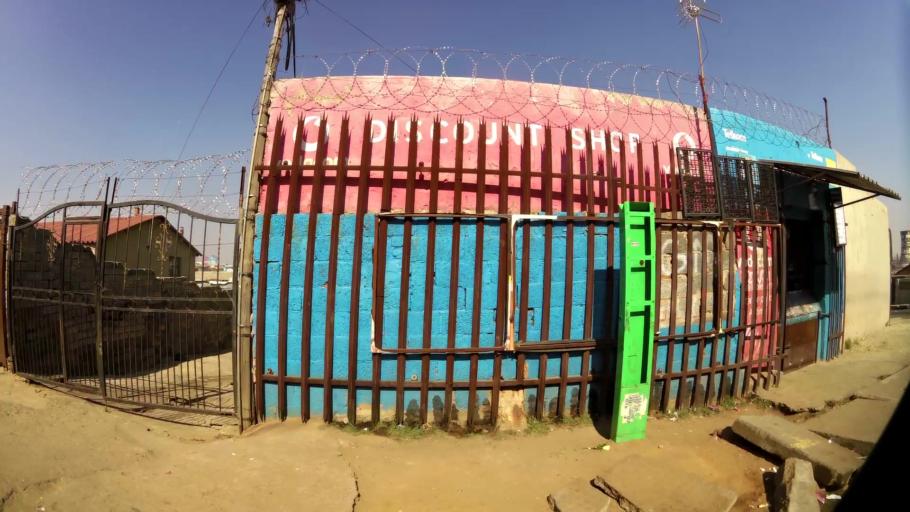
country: ZA
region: Gauteng
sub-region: City of Johannesburg Metropolitan Municipality
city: Soweto
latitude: -26.2511
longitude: 27.9394
